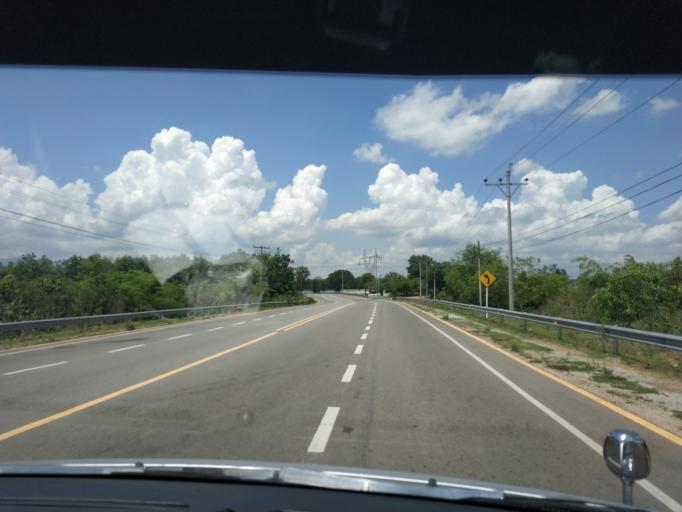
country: MM
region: Mon
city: Kyaikto
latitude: 17.3323
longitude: 97.0353
